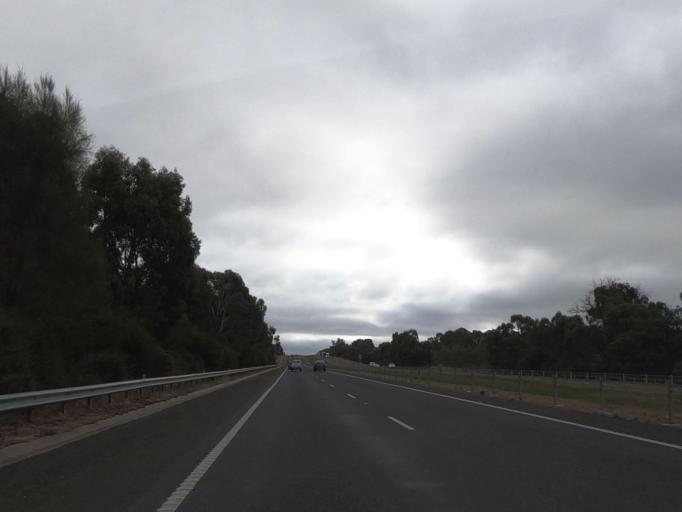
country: AU
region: Victoria
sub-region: Mount Alexander
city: Castlemaine
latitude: -37.0664
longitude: 144.3084
